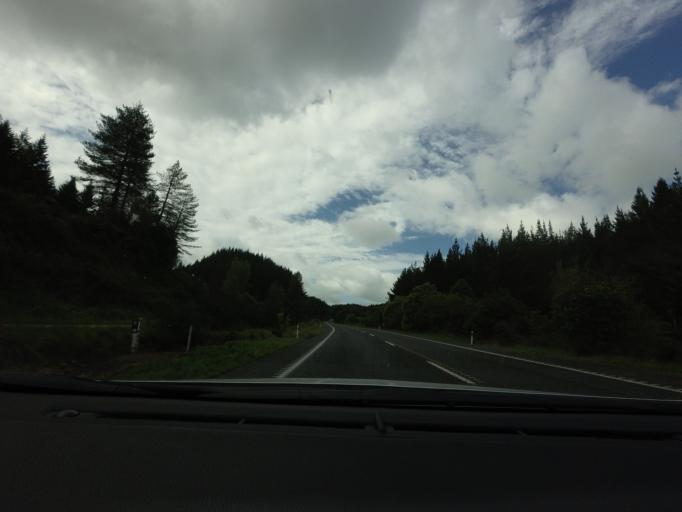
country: NZ
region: Bay of Plenty
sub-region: Rotorua District
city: Rotorua
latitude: -38.1975
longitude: 176.2592
